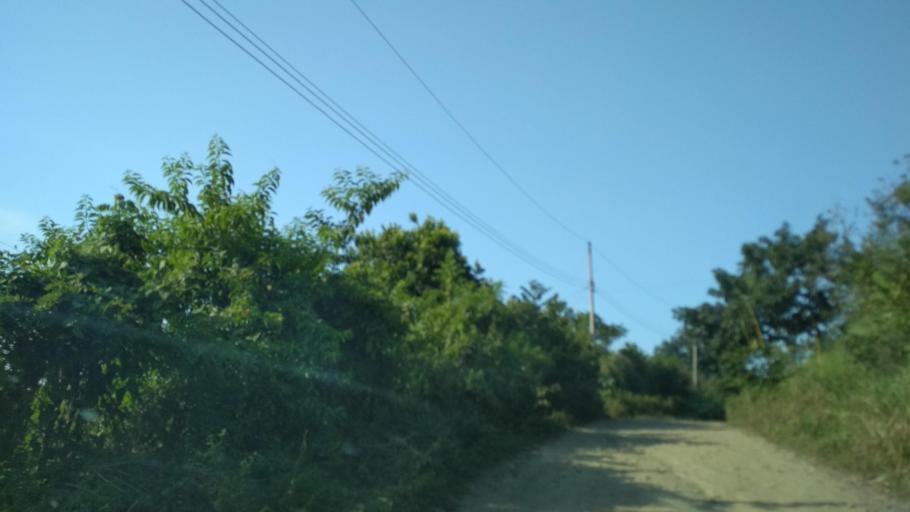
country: MX
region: Puebla
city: San Jose Acateno
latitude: 20.2156
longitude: -97.2641
